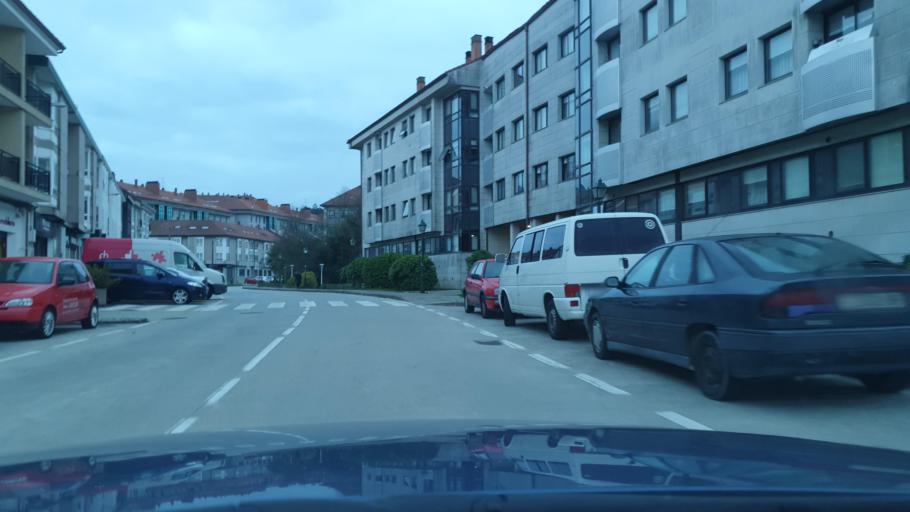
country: ES
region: Galicia
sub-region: Provincia da Coruna
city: Santiago de Compostela
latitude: 42.8852
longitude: -8.5315
